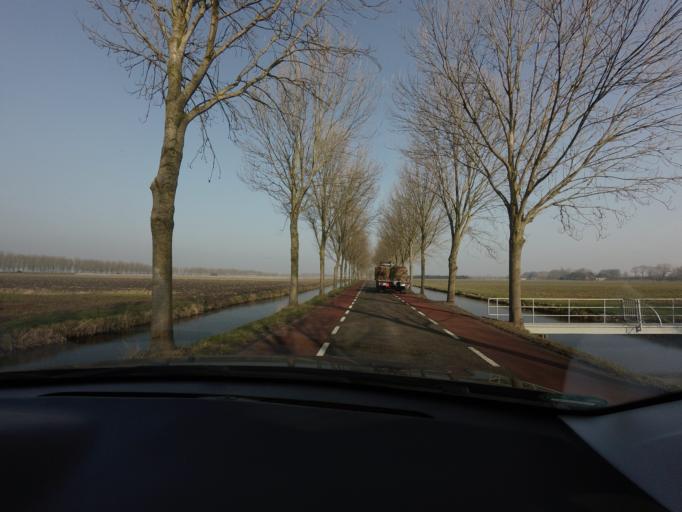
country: NL
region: North Holland
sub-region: Gemeente Beemster
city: Halfweg
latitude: 52.5579
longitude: 4.9684
